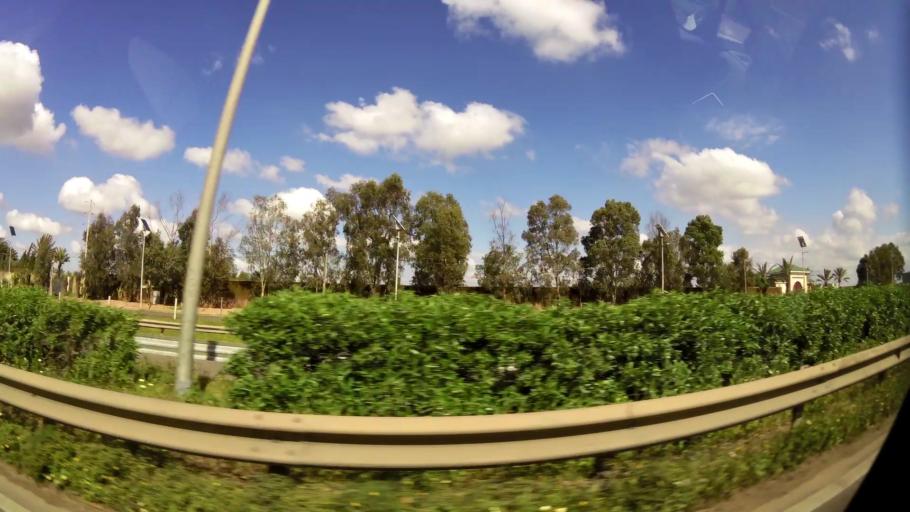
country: MA
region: Chaouia-Ouardigha
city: Nouaseur
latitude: 33.4111
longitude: -7.6263
